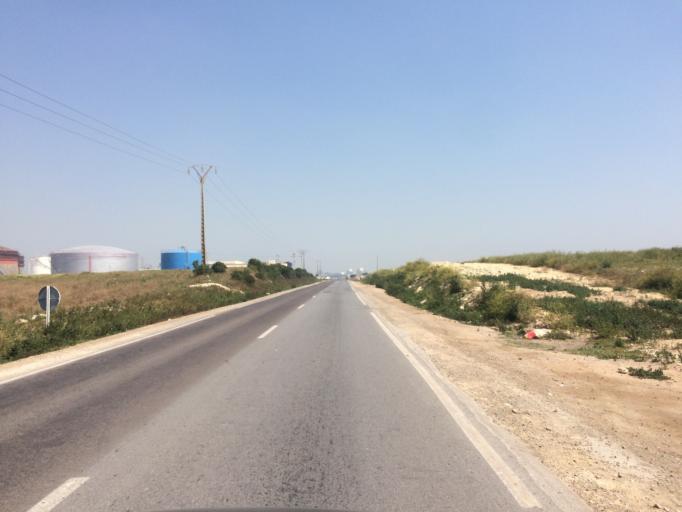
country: MA
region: Doukkala-Abda
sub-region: El-Jadida
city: Moulay Abdallah
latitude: 33.1492
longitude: -8.6061
